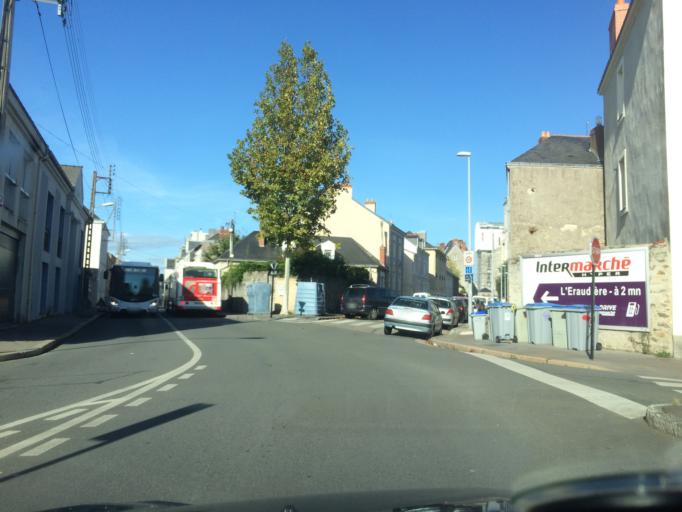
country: FR
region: Pays de la Loire
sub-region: Departement de la Loire-Atlantique
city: Nantes
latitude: 47.2275
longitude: -1.5453
